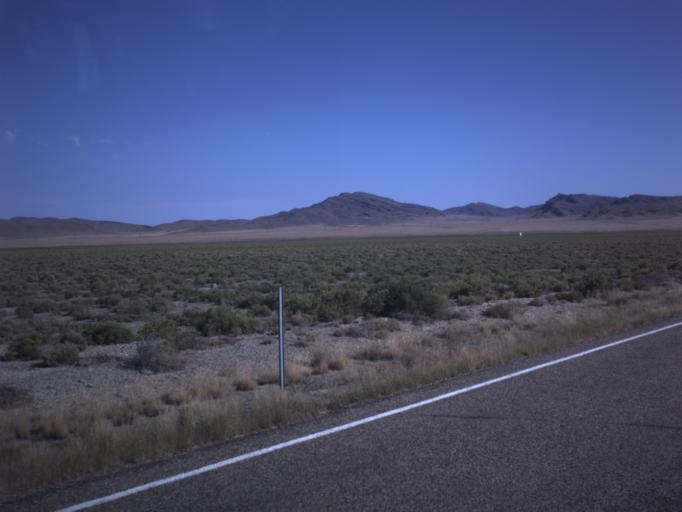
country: US
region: Utah
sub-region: Beaver County
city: Milford
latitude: 38.7007
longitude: -112.9725
